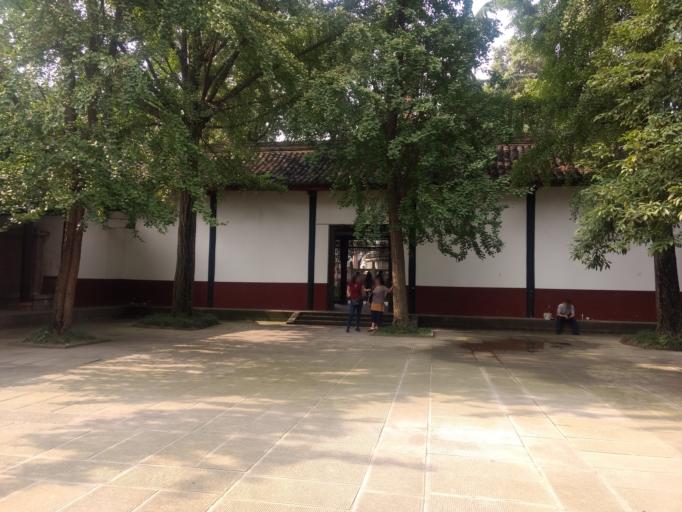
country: CN
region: Sichuan
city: Chengdu
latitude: 30.6774
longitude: 104.0704
